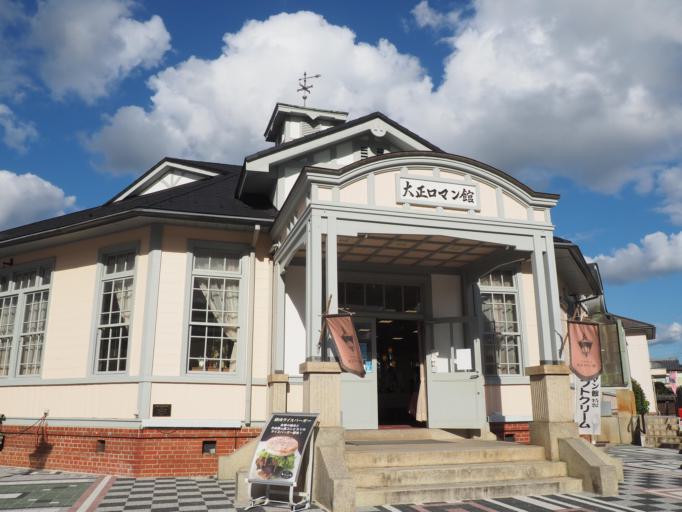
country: JP
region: Hyogo
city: Sasayama
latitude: 35.0759
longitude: 135.2170
